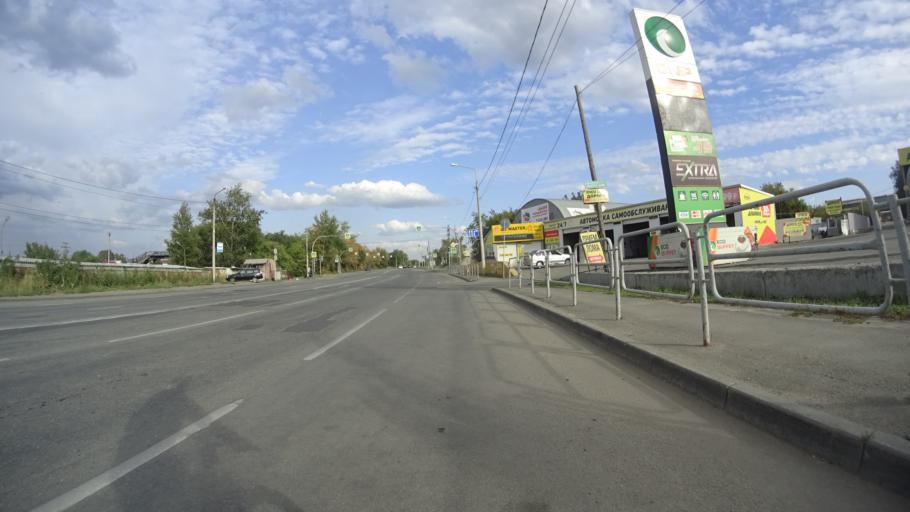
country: RU
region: Chelyabinsk
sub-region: Gorod Chelyabinsk
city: Chelyabinsk
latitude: 55.1973
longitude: 61.3699
